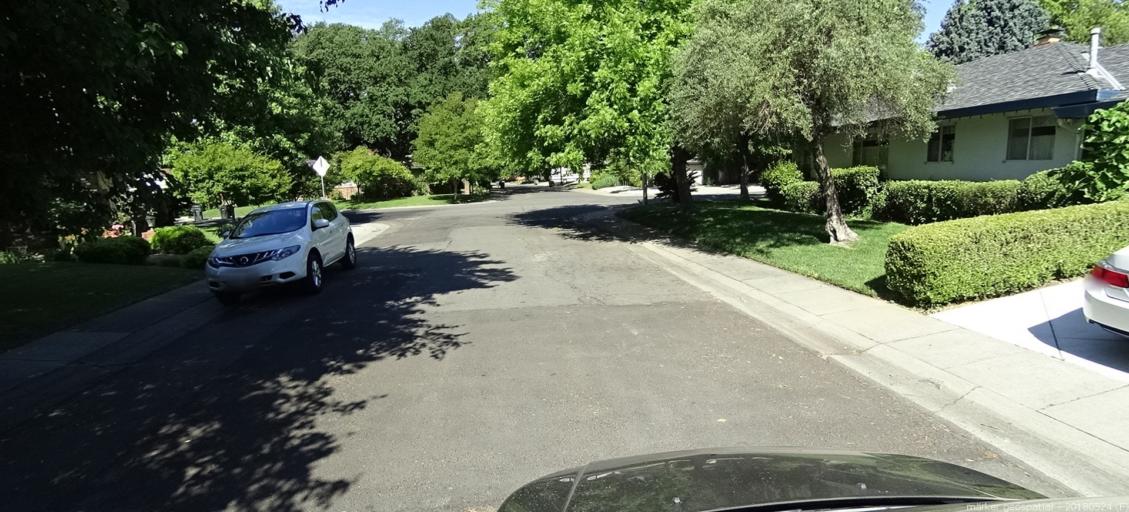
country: US
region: California
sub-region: Sacramento County
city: Sacramento
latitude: 38.6023
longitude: -121.4597
